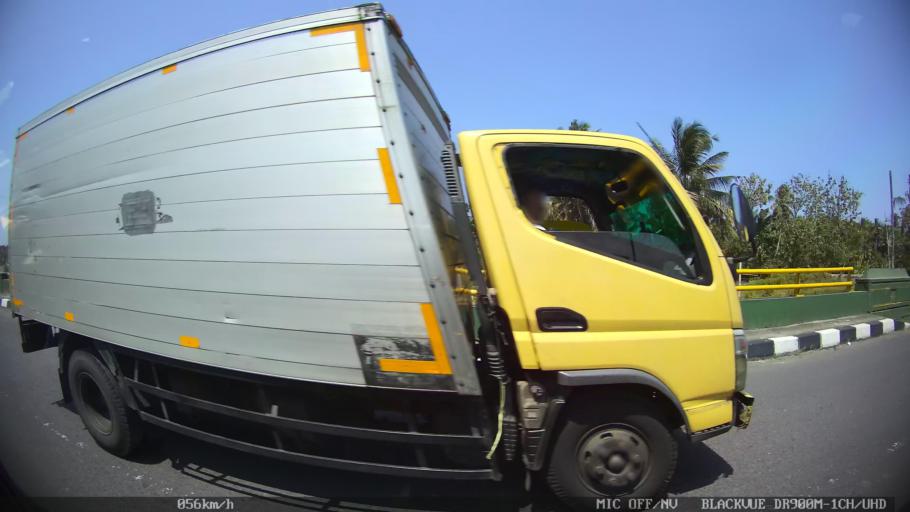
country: ID
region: Daerah Istimewa Yogyakarta
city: Srandakan
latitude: -7.9444
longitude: 110.1721
